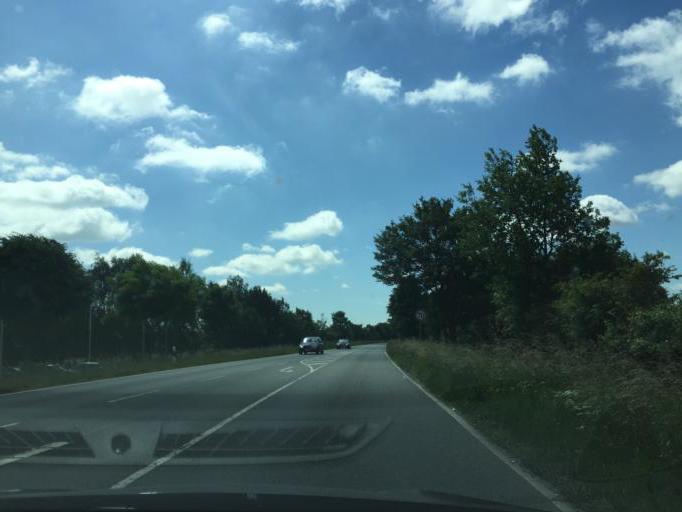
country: DE
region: Schleswig-Holstein
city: Harrislee
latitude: 54.7937
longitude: 9.3721
